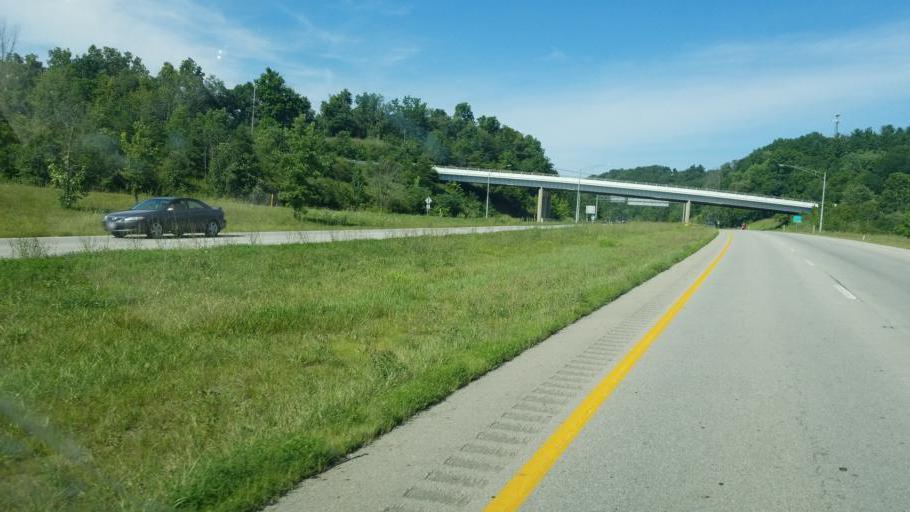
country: US
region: Ohio
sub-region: Athens County
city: Athens
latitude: 39.3145
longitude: -82.0971
